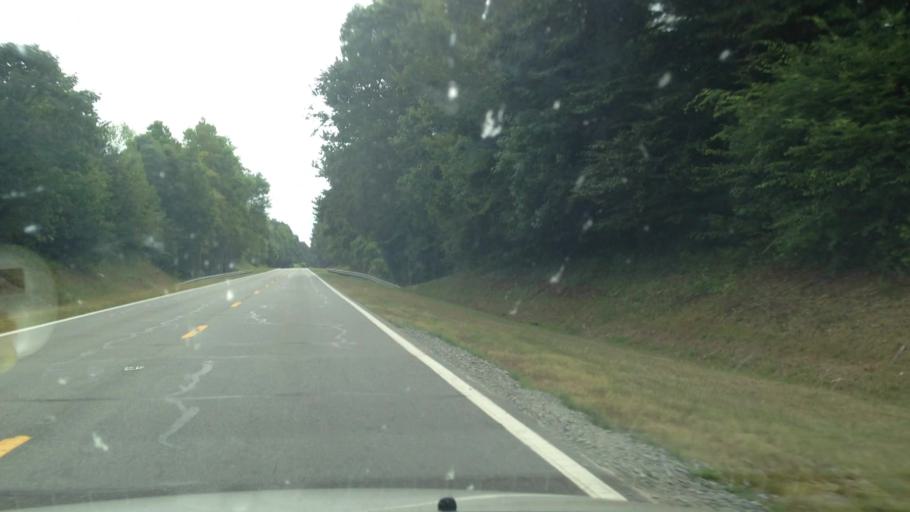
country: US
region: North Carolina
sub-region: Rockingham County
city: Madison
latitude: 36.3798
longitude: -79.8727
